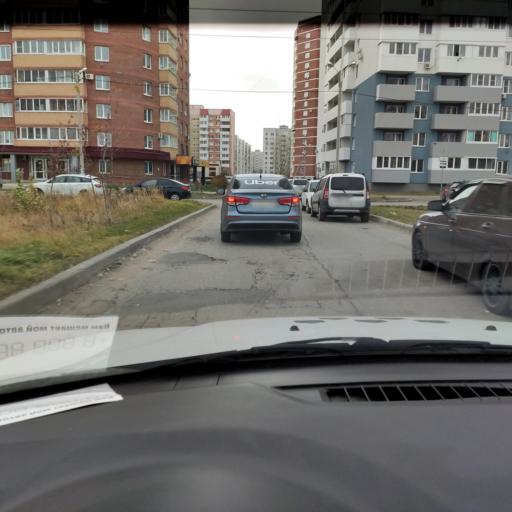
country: RU
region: Samara
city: Tol'yatti
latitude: 53.5413
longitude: 49.3938
